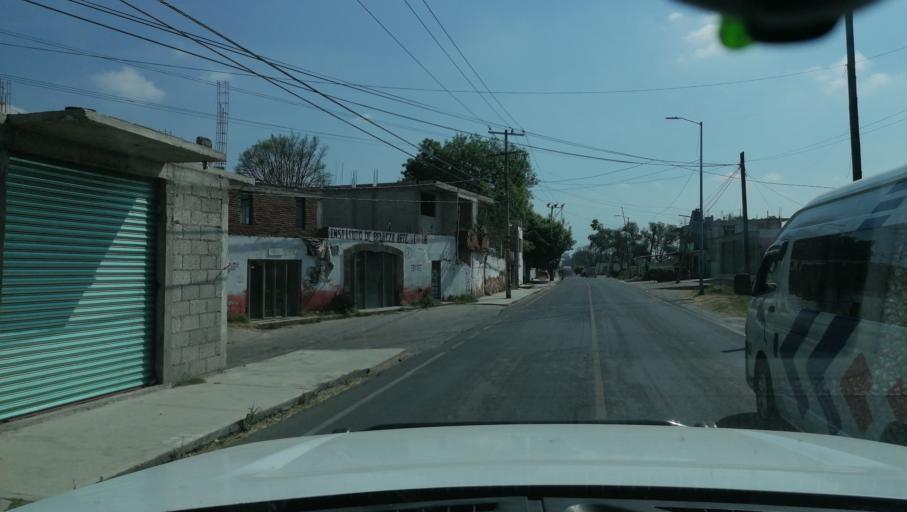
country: MX
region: Tlaxcala
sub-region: Tetlatlahuca
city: Tetlatlahuca
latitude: 19.2313
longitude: -98.2942
